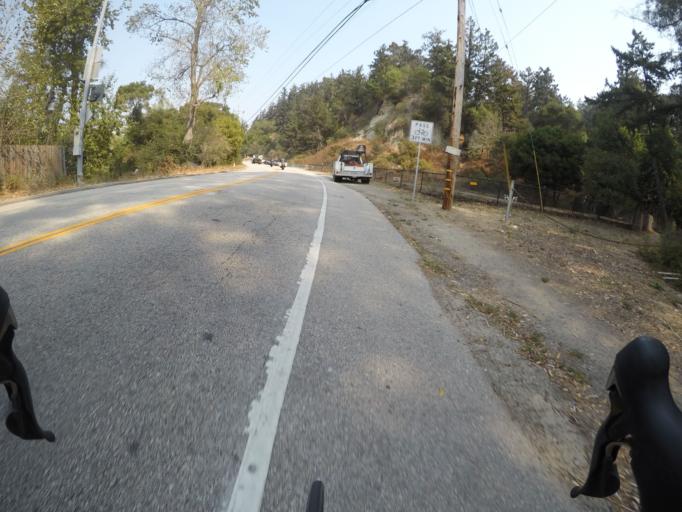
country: US
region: California
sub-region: Santa Cruz County
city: Pasatiempo
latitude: 36.9918
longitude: -122.0115
